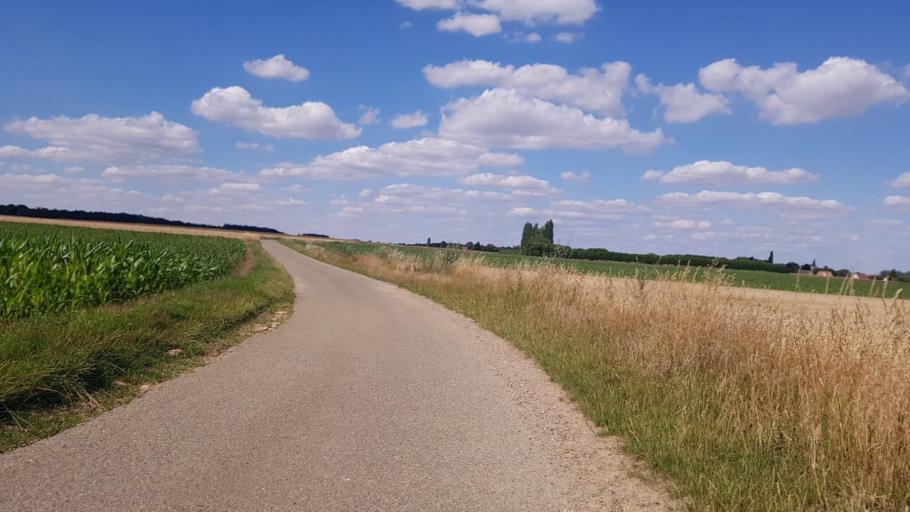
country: FR
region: Picardie
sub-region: Departement de l'Oise
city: Ver-sur-Launette
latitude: 49.0983
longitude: 2.6764
